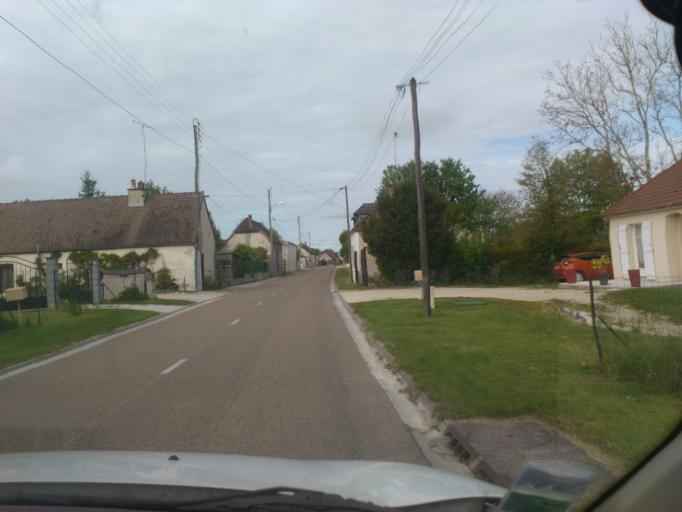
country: FR
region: Champagne-Ardenne
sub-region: Departement de l'Aube
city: Marigny-le-Chatel
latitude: 48.3577
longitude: 3.7045
